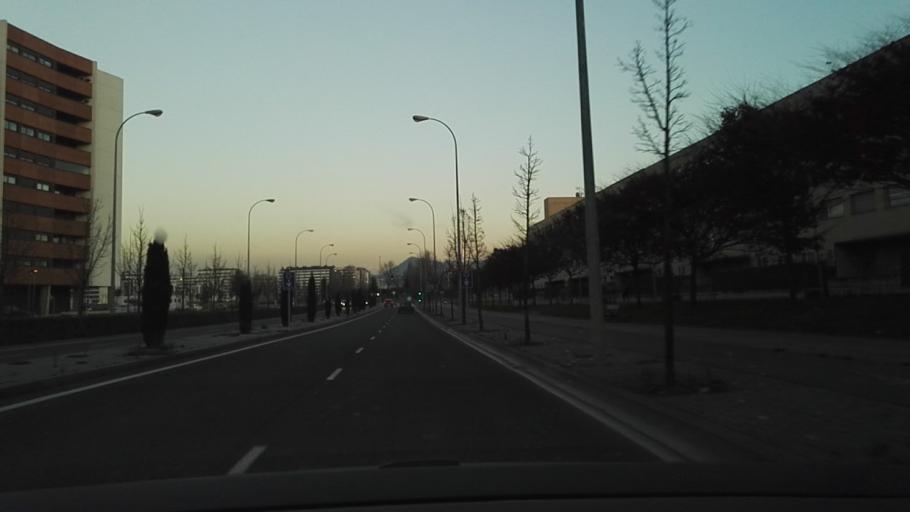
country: ES
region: Navarre
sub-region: Provincia de Navarra
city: Burlata
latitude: 42.8148
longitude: -1.6177
